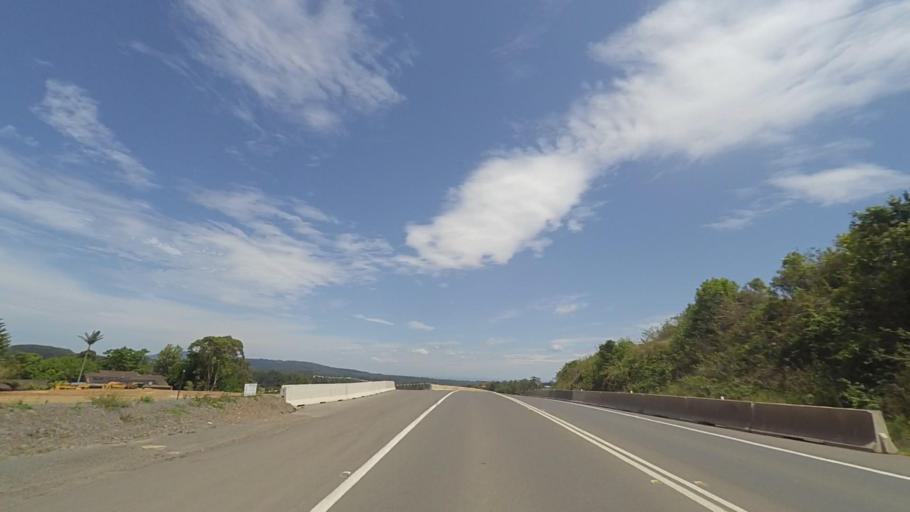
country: AU
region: New South Wales
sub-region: Shoalhaven Shire
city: Berry
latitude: -34.7579
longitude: 150.7443
